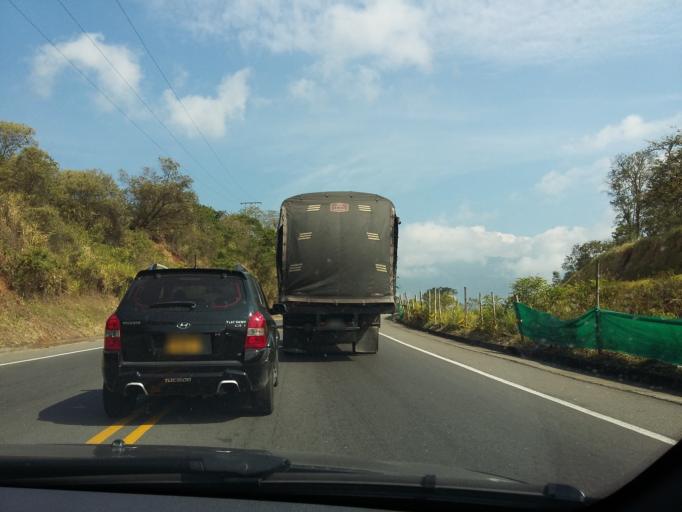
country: CO
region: Tolima
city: Ibague
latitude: 4.4095
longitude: -75.1859
